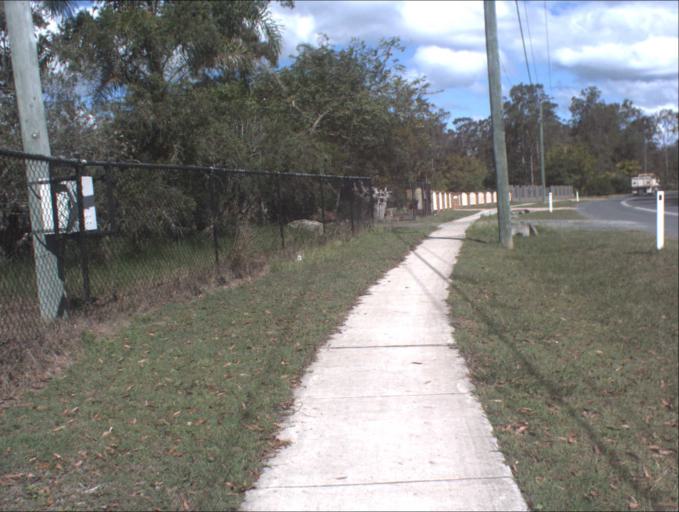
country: AU
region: Queensland
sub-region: Logan
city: Chambers Flat
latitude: -27.7449
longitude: 153.0538
